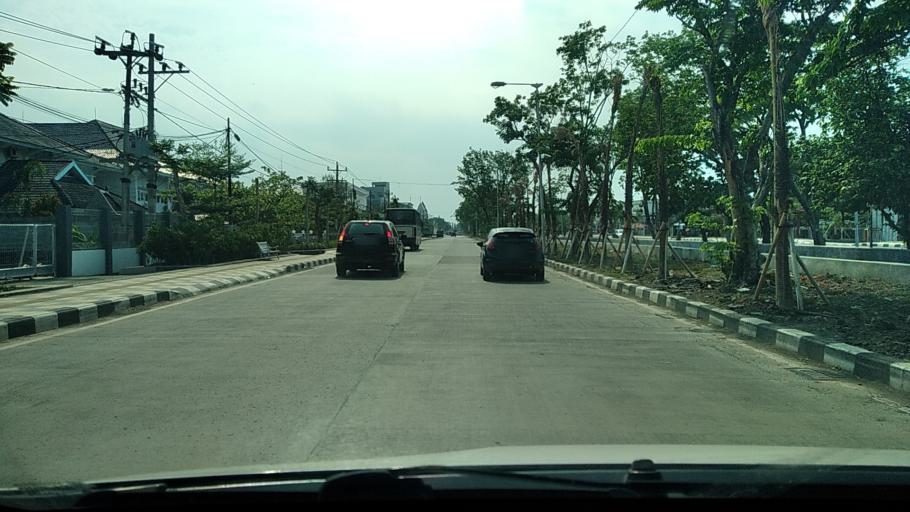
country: ID
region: Central Java
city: Semarang
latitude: -6.9616
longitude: 110.3984
